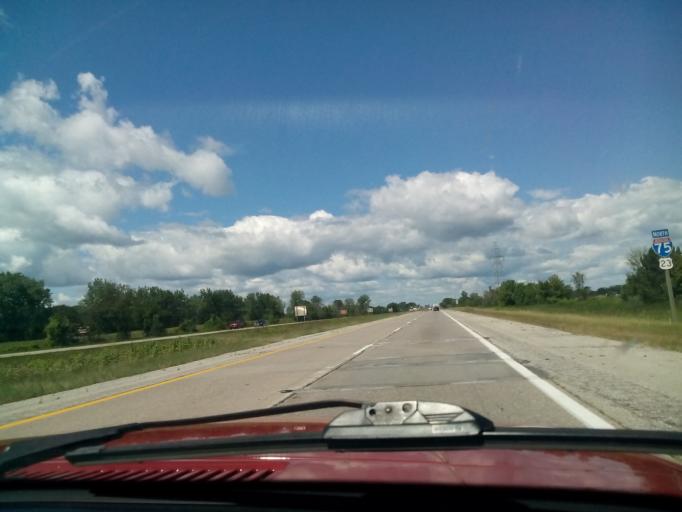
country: US
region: Michigan
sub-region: Bay County
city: Bay City
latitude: 43.6291
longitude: -83.9607
